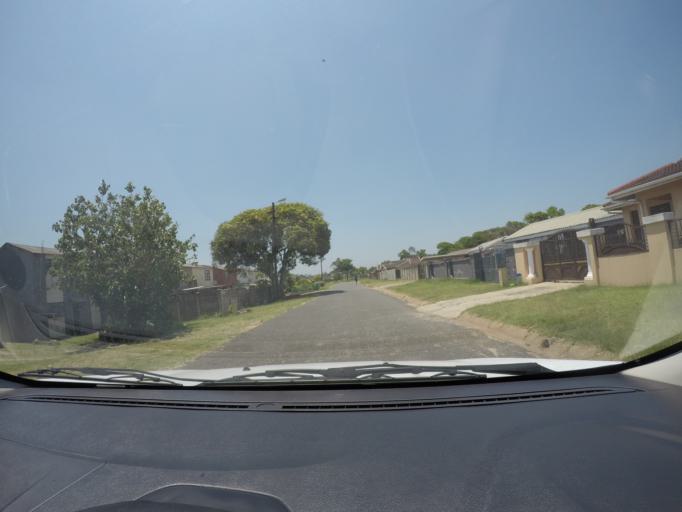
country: ZA
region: KwaZulu-Natal
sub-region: uThungulu District Municipality
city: eSikhawini
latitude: -28.8819
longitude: 31.8912
